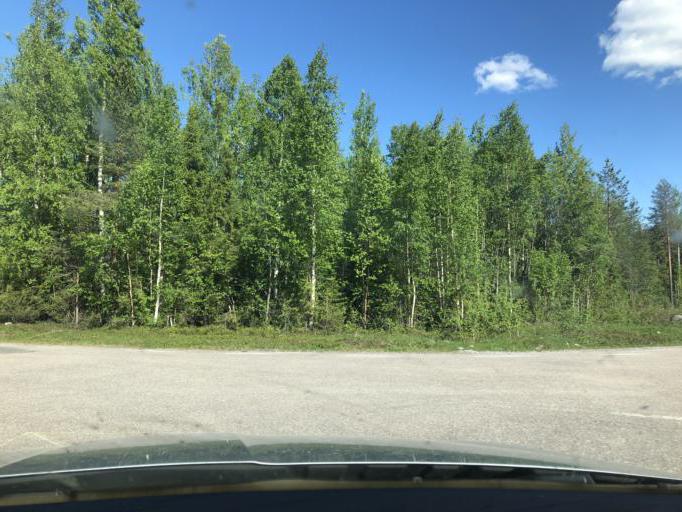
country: SE
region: Norrbotten
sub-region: Kalix Kommun
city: Kalix
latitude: 66.0581
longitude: 23.2033
